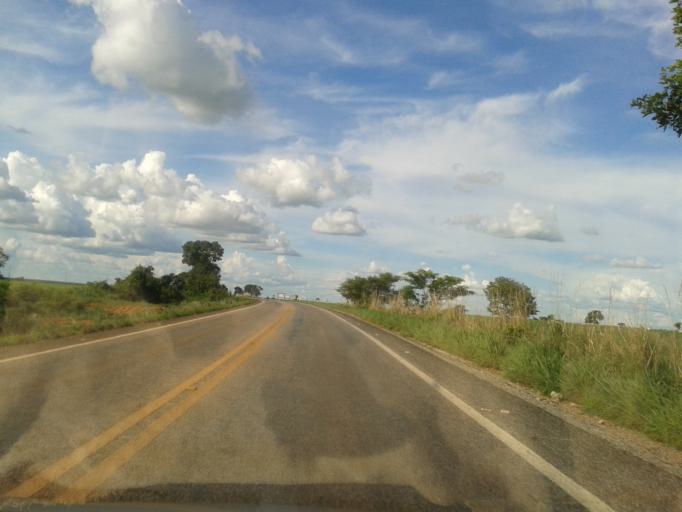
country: BR
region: Goias
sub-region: Mozarlandia
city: Mozarlandia
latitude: -14.5310
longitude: -50.4862
